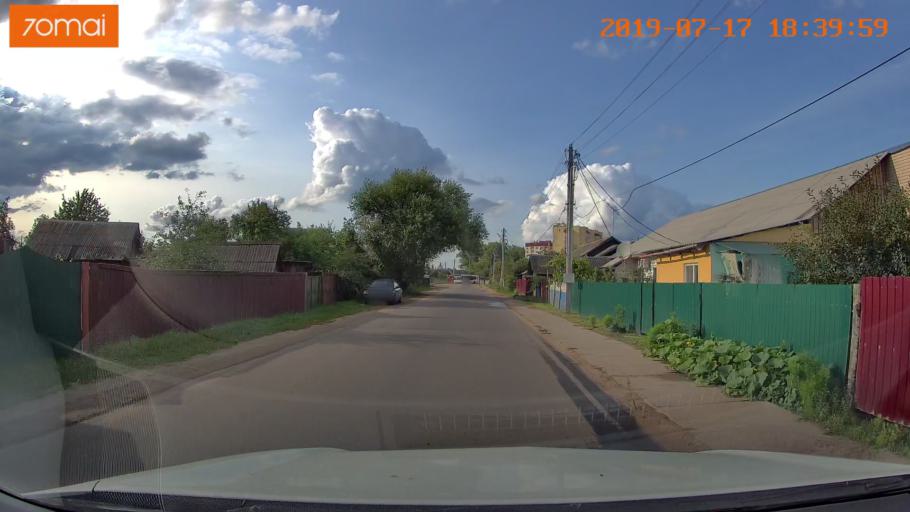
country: BY
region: Mogilev
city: Asipovichy
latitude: 53.2998
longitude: 28.6541
